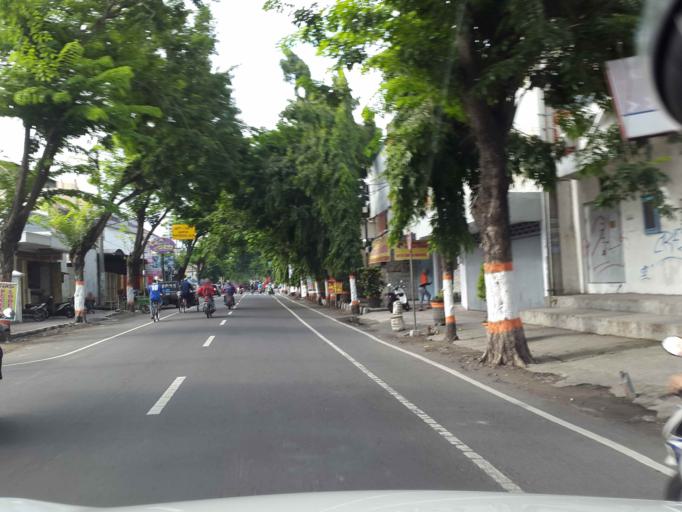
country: ID
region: East Java
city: Soko
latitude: -7.4763
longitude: 112.4320
